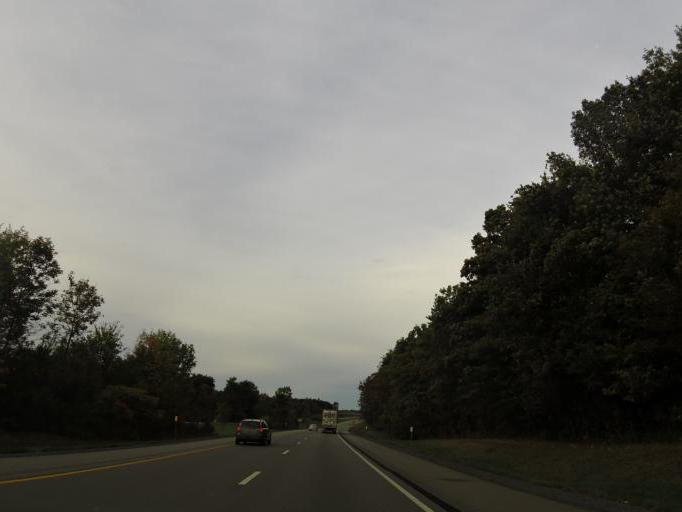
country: US
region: New York
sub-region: Erie County
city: Angola
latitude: 42.6065
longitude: -79.0255
